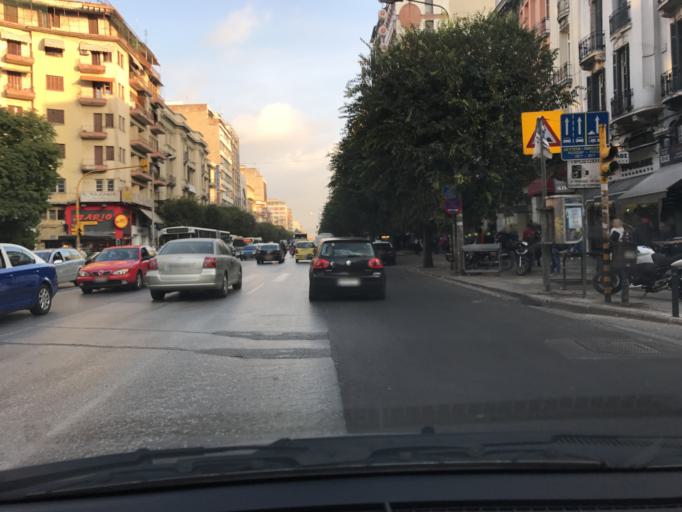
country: GR
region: Central Macedonia
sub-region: Nomos Thessalonikis
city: Thessaloniki
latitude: 40.6389
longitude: 22.9382
